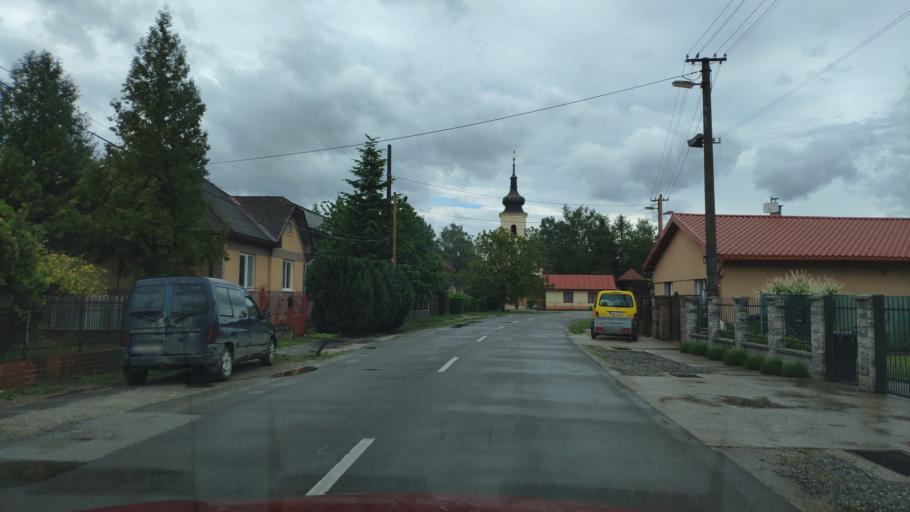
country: SK
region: Kosicky
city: Moldava nad Bodvou
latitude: 48.5754
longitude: 21.1208
